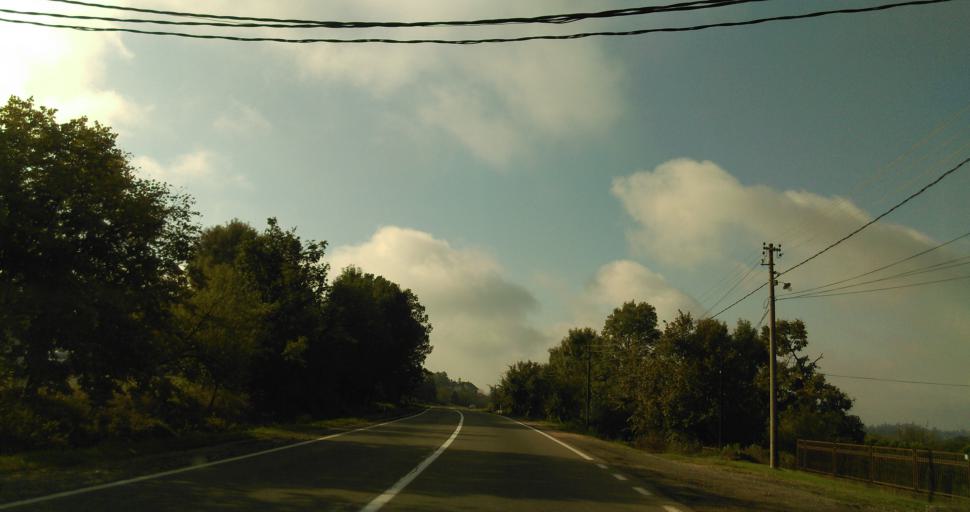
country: RS
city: Vranic
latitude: 44.5989
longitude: 20.3518
